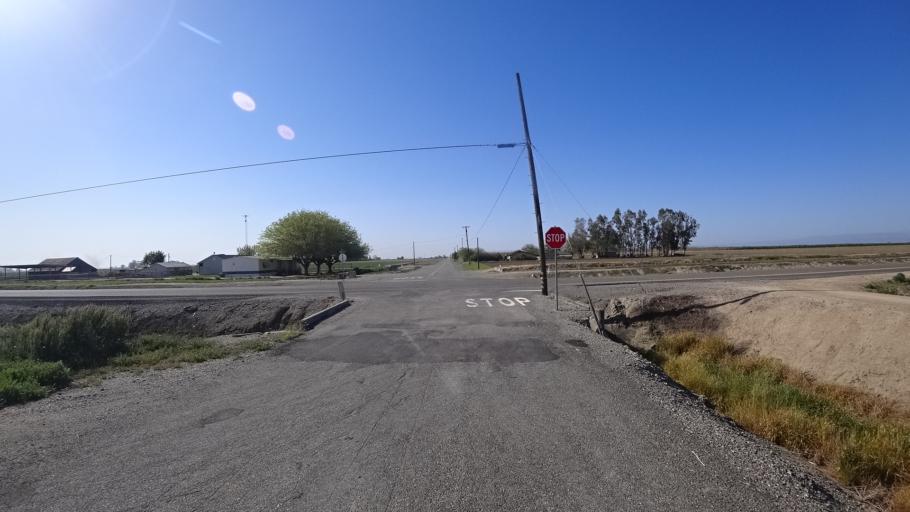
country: US
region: California
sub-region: Glenn County
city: Willows
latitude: 39.5823
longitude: -122.1170
